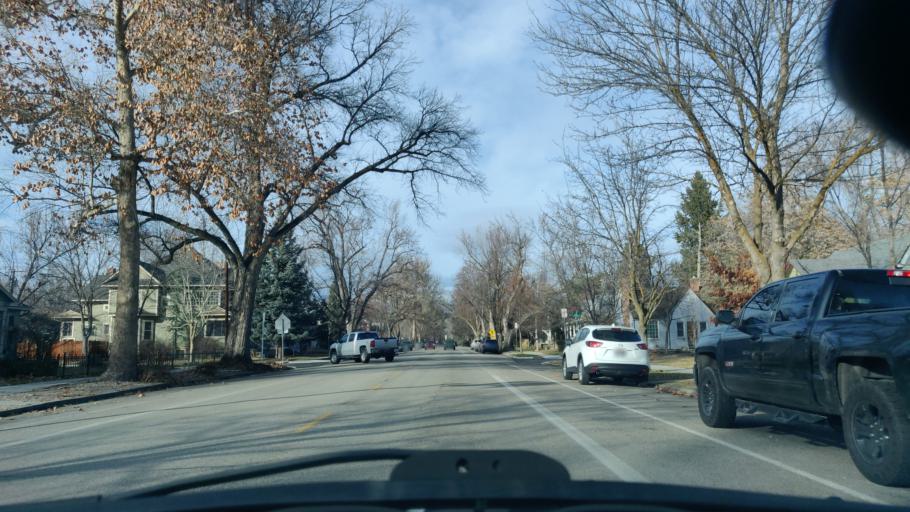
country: US
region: Idaho
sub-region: Ada County
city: Boise
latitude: 43.6270
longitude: -116.2058
